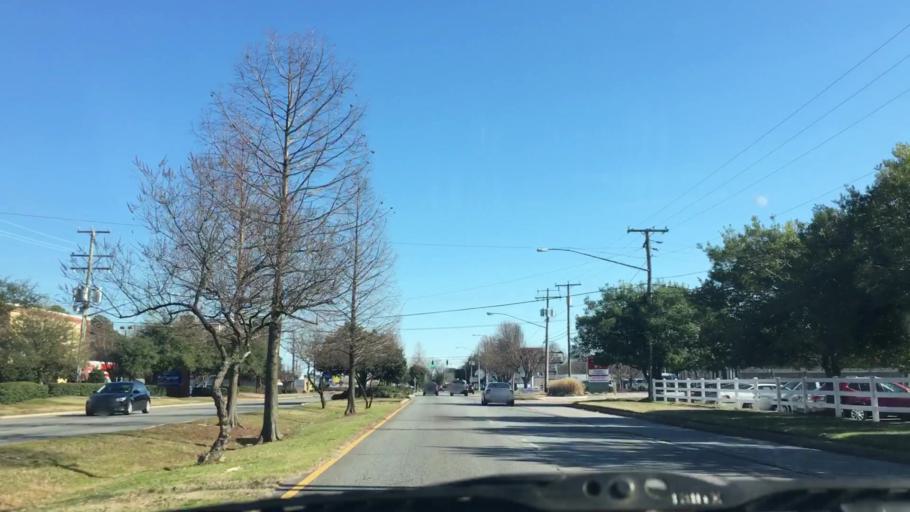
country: US
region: Virginia
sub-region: City of Norfolk
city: Norfolk
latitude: 36.9164
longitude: -76.2268
